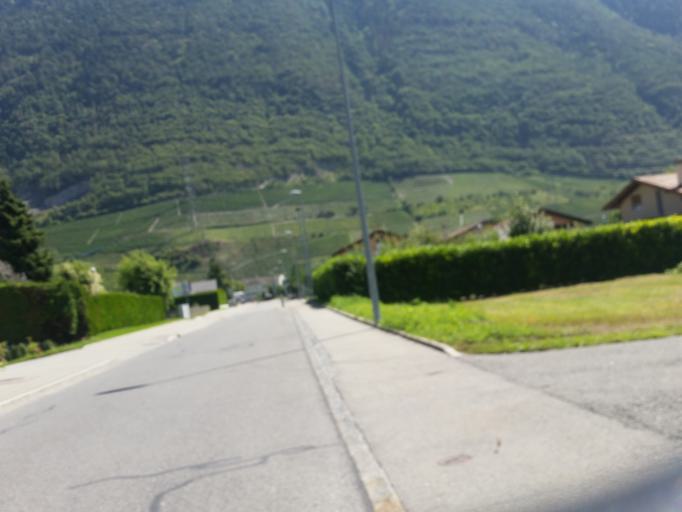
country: CH
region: Valais
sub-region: Martigny District
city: Charrat-les-Chenes
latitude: 46.1236
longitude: 7.1318
